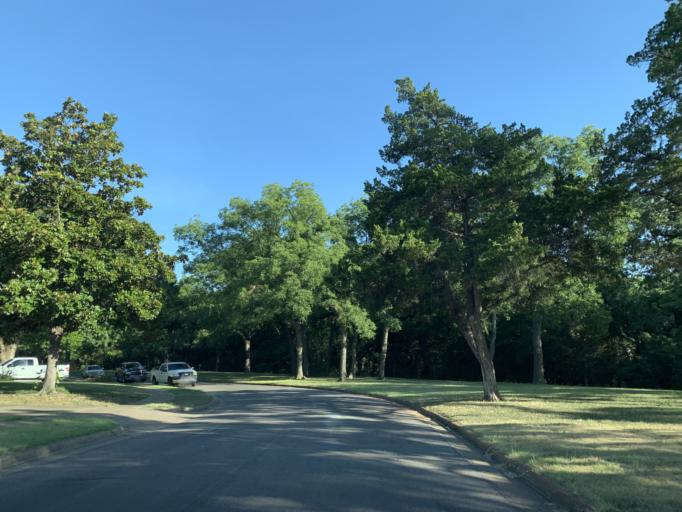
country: US
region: Texas
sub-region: Dallas County
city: Cockrell Hill
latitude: 32.7099
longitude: -96.8995
